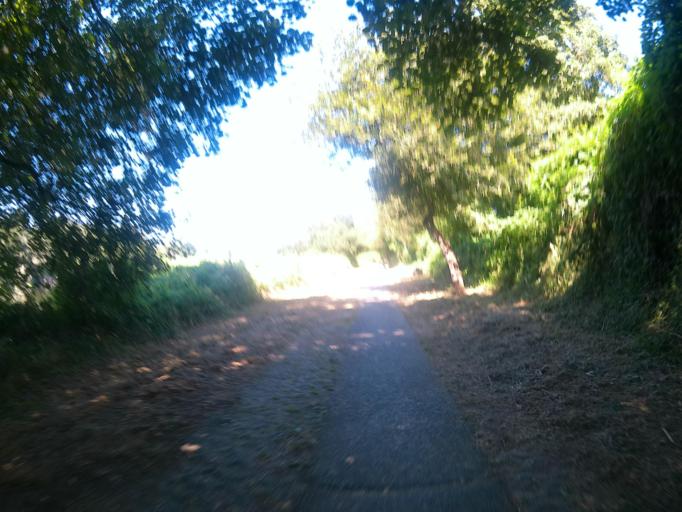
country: PT
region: Viana do Castelo
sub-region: Ponte de Lima
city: Ponte de Lima
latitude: 41.7634
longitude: -8.6034
